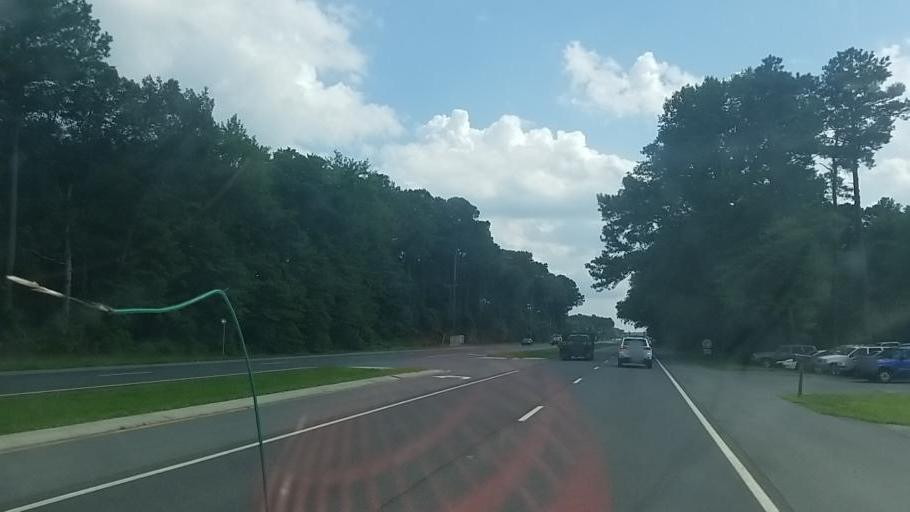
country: US
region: Delaware
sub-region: Sussex County
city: Selbyville
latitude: 38.4723
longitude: -75.2348
